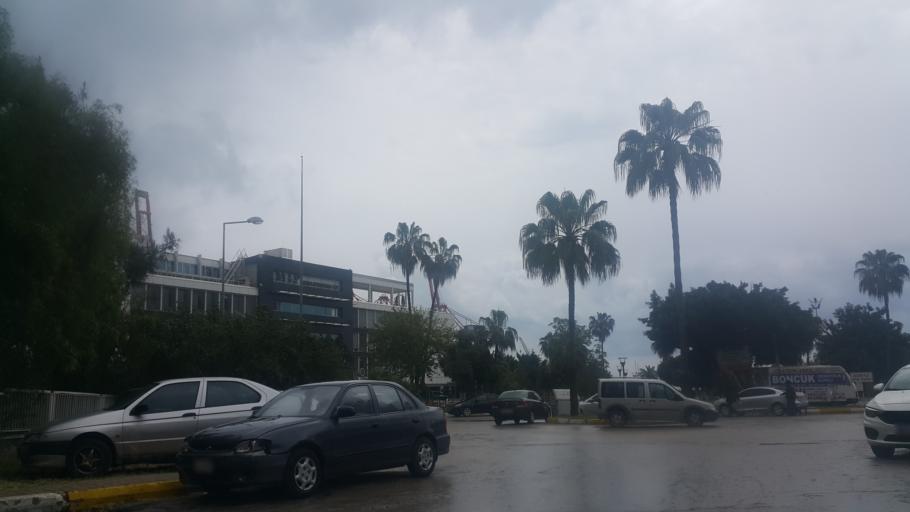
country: TR
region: Mersin
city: Mercin
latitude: 36.8005
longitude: 34.6354
